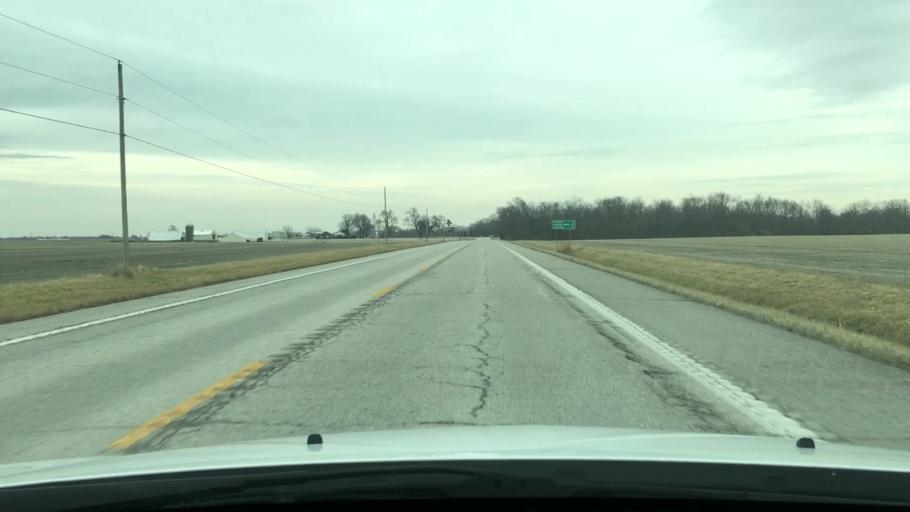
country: US
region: Missouri
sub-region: Audrain County
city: Vandalia
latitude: 39.2791
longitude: -91.5709
